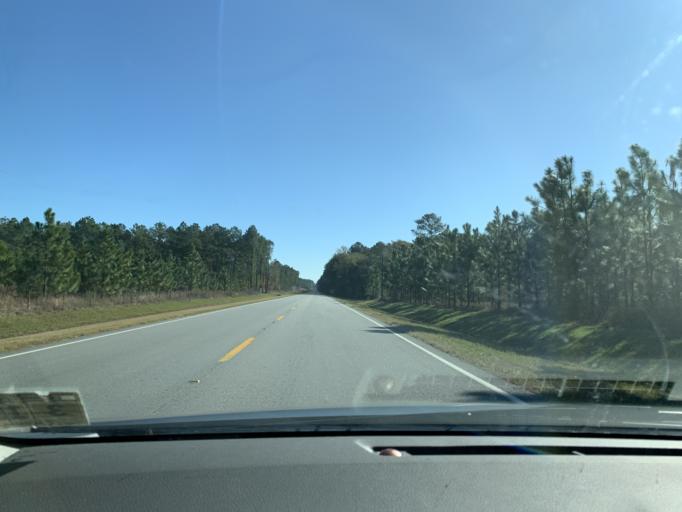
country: US
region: Georgia
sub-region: Ben Hill County
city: Fitzgerald
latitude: 31.7759
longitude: -83.0663
